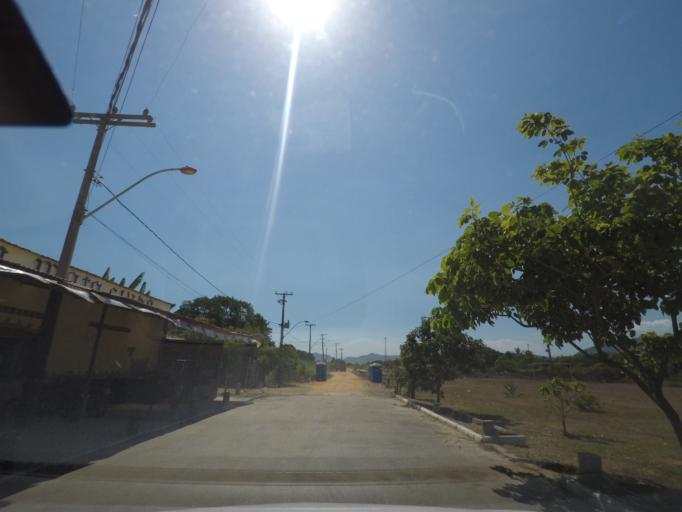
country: BR
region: Rio de Janeiro
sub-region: Marica
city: Marica
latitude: -22.9722
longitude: -42.9271
